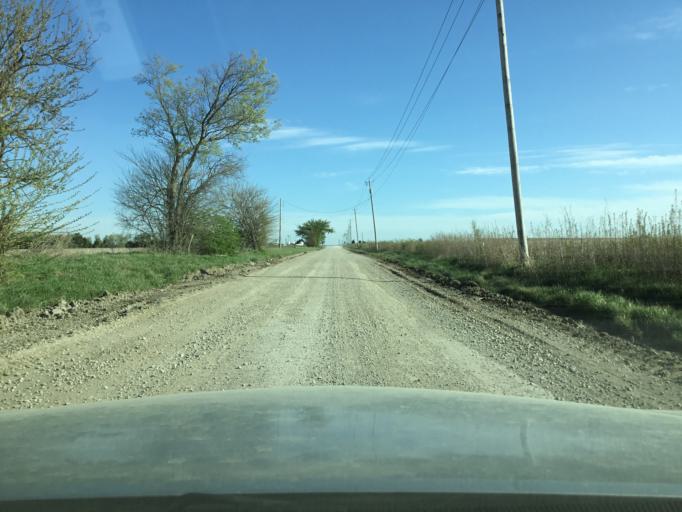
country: US
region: Kansas
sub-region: Neosho County
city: Chanute
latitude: 37.6573
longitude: -95.4893
